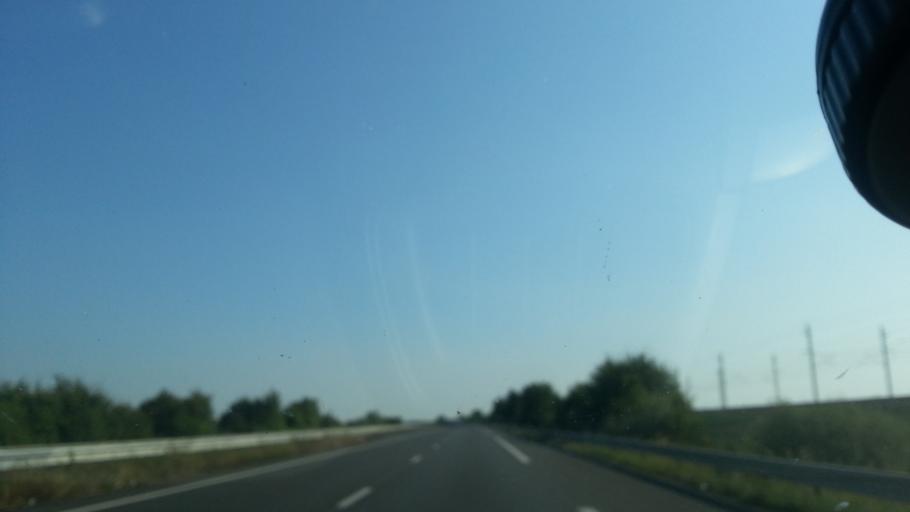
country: FR
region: Centre
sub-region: Departement d'Indre-et-Loire
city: La Celle-Saint-Avant
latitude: 47.0419
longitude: 0.5811
